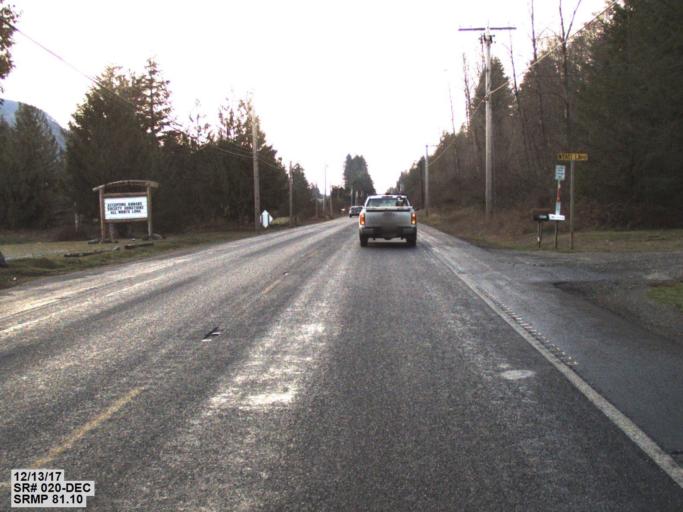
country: US
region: Washington
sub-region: Skagit County
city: Sedro-Woolley
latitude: 48.5285
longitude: -121.9127
